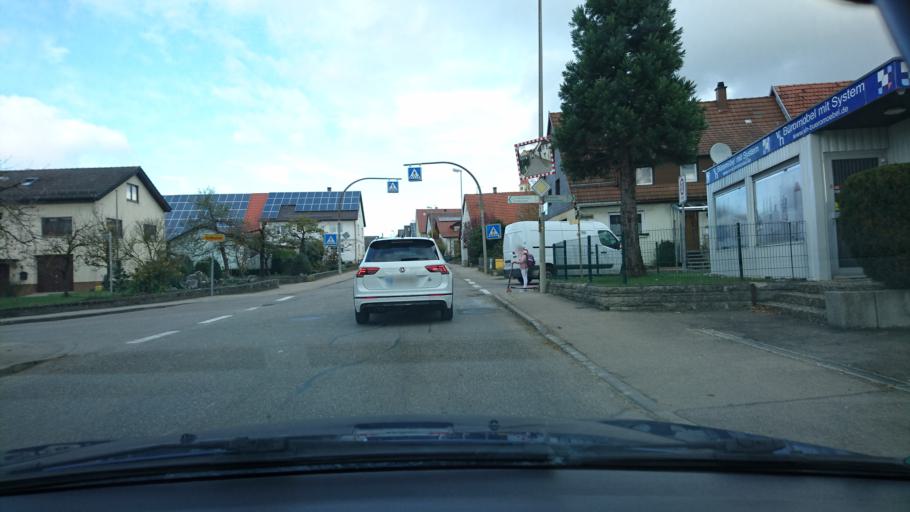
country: DE
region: Baden-Wuerttemberg
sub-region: Regierungsbezirk Stuttgart
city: Neresheim
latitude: 48.7913
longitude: 10.2654
